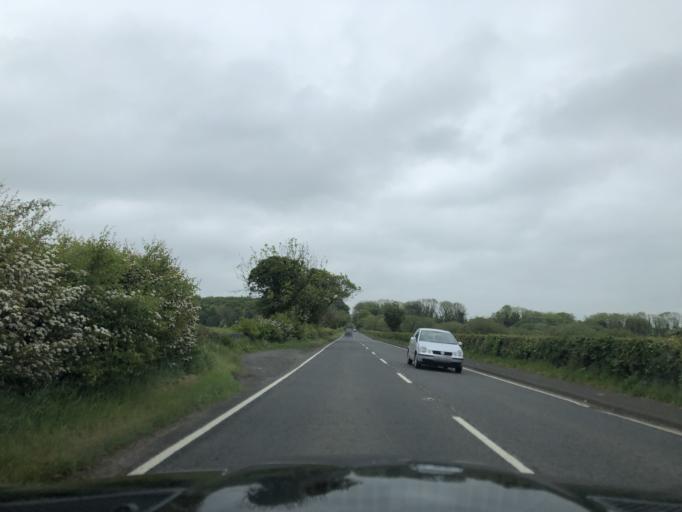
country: GB
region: Northern Ireland
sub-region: Down District
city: Downpatrick
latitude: 54.3127
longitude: -5.7383
